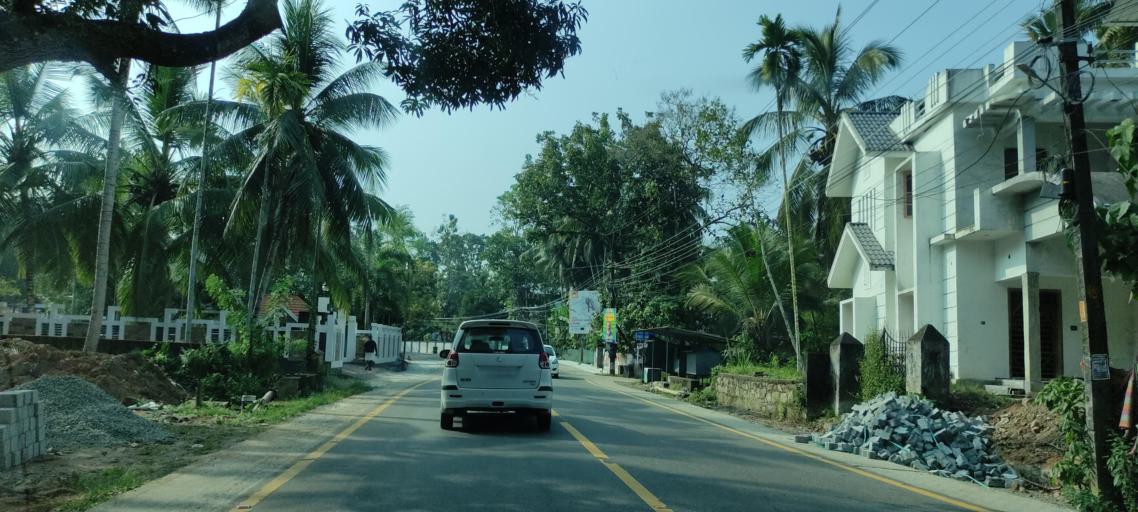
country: IN
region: Kerala
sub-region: Pattanamtitta
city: Tiruvalla
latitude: 9.3704
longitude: 76.5256
